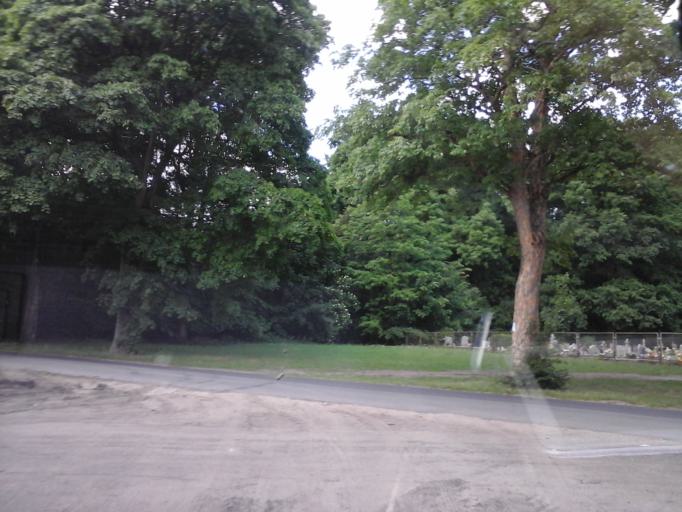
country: PL
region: Lubusz
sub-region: Powiat strzelecko-drezdenecki
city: Dobiegniew
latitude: 53.0574
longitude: 15.7593
